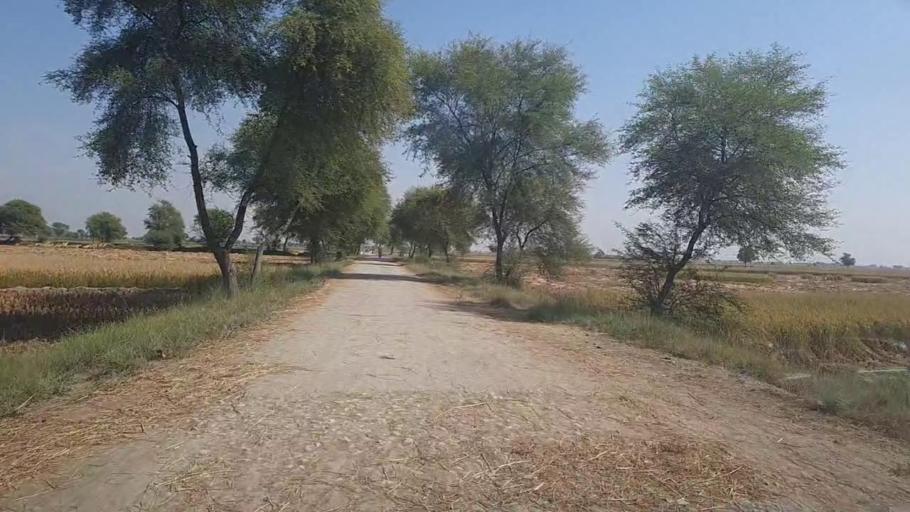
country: PK
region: Sindh
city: Thul
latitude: 28.2483
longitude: 68.8165
